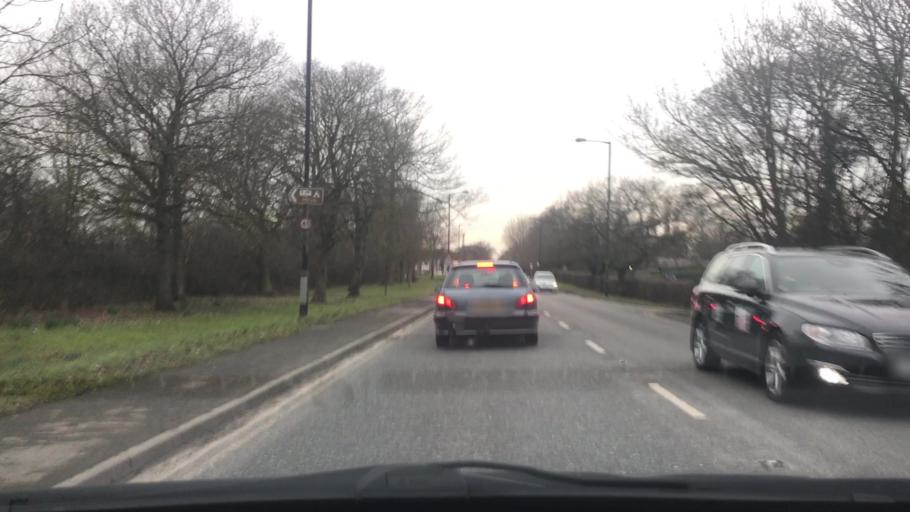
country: GB
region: England
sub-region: North Yorkshire
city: Knaresborough
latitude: 53.9847
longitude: -1.4933
